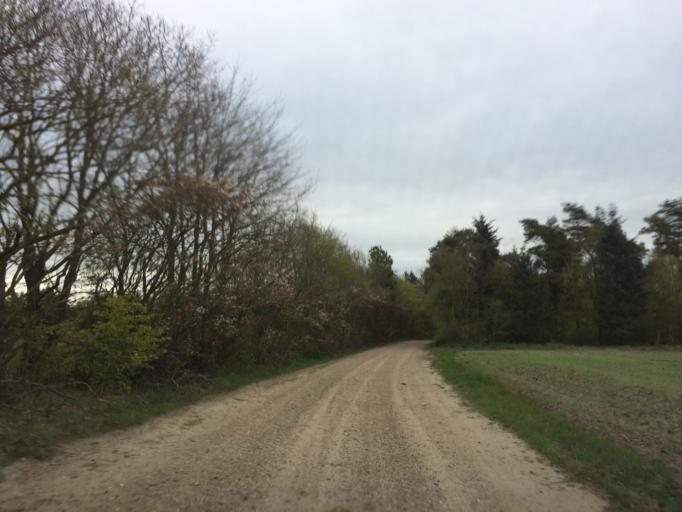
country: DK
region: Central Jutland
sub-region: Viborg Kommune
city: Karup
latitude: 56.3453
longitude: 9.1235
